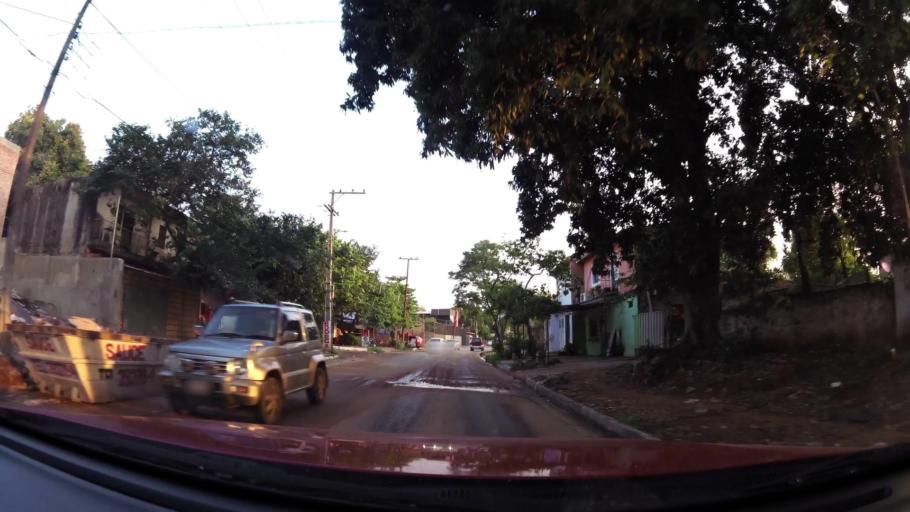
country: PY
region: Central
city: Lambare
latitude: -25.3498
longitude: -57.6007
